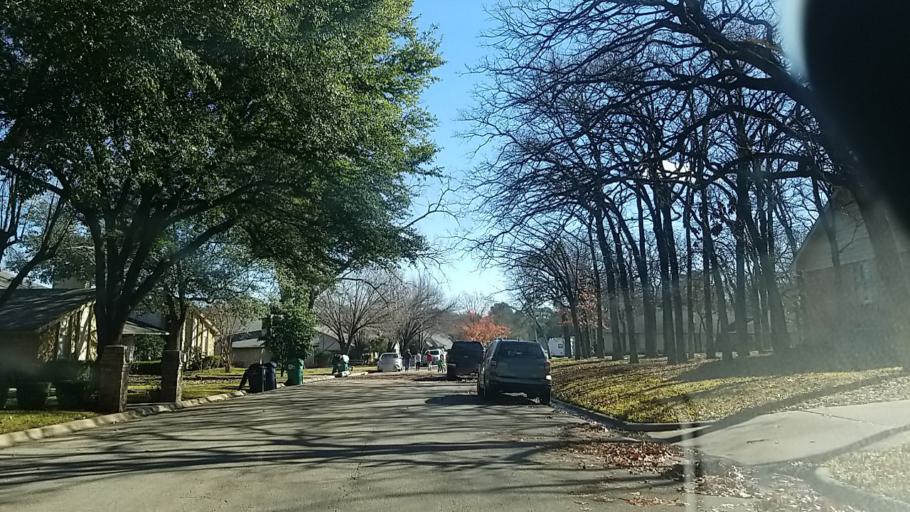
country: US
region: Texas
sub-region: Denton County
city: Denton
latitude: 33.1903
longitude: -97.1167
